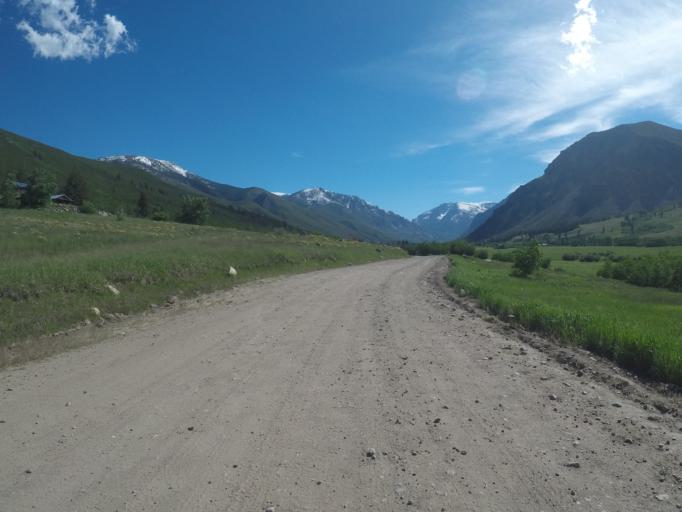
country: US
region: Montana
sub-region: Stillwater County
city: Absarokee
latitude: 45.2764
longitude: -109.5500
